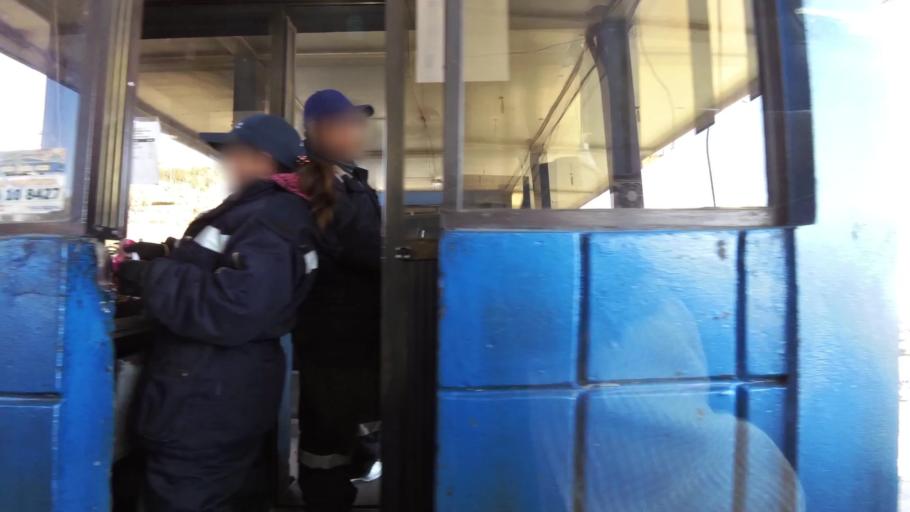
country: BO
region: La Paz
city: La Paz
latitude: -16.5007
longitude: -68.1628
